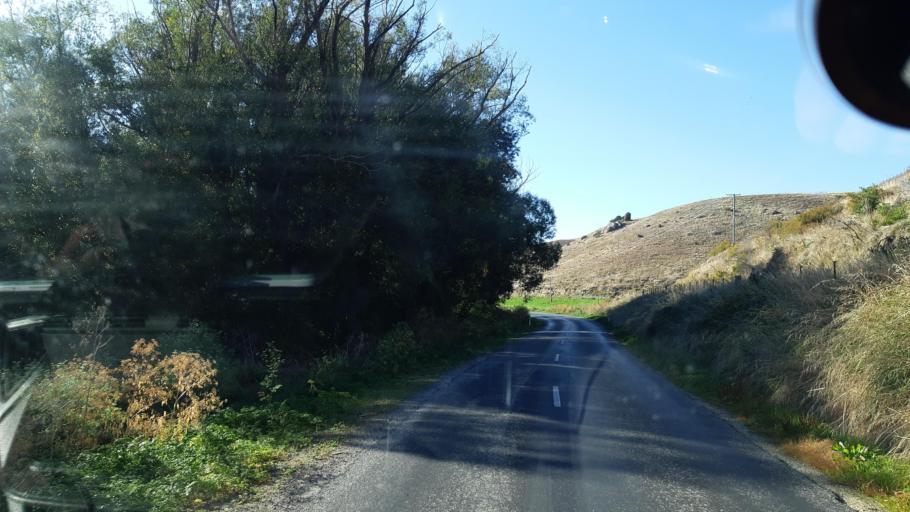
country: NZ
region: Otago
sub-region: Queenstown-Lakes District
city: Wanaka
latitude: -44.8819
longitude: 169.3568
